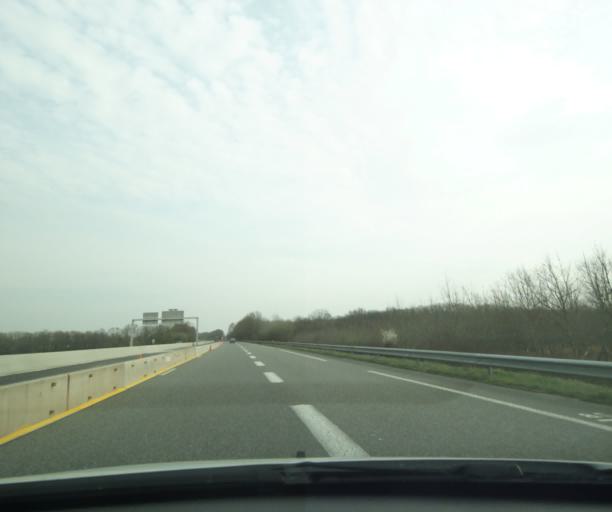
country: FR
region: Aquitaine
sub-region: Departement des Pyrenees-Atlantiques
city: Artix
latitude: 43.3945
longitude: -0.5458
